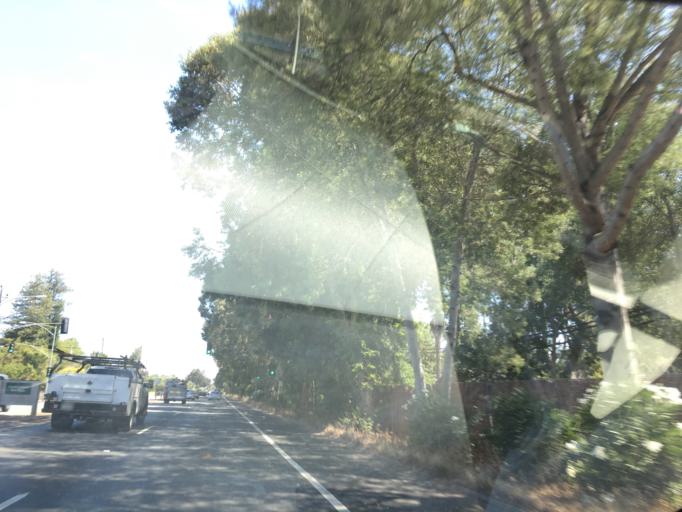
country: US
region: California
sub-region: Santa Clara County
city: Loyola
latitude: 37.3579
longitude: -122.0944
